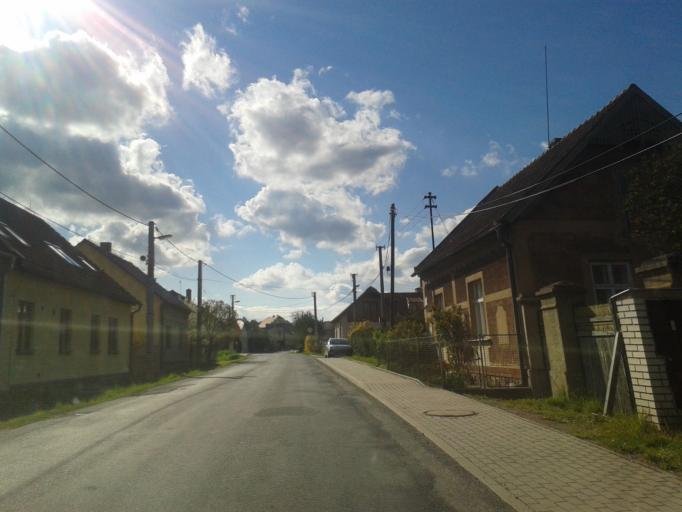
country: CZ
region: Central Bohemia
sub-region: Okres Beroun
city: Lodenice
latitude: 50.0108
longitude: 14.1196
